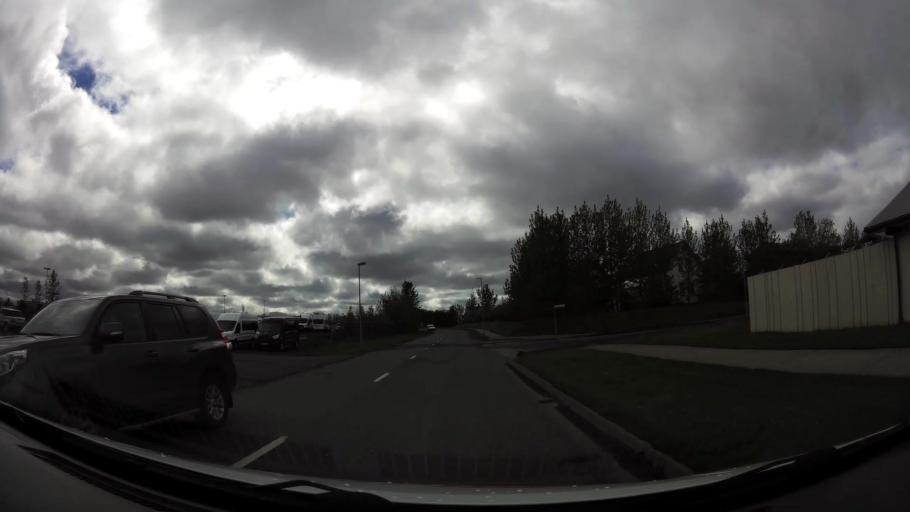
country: IS
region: Capital Region
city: Kopavogur
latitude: 64.1342
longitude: -21.9468
